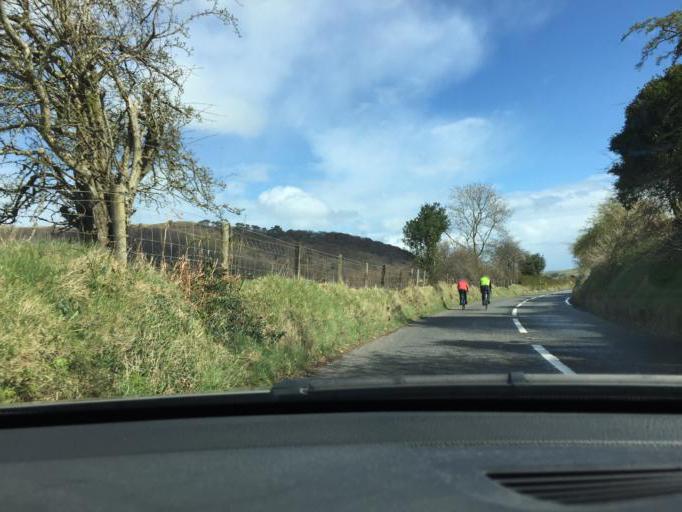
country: GB
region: Northern Ireland
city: Cushendall
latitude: 55.1206
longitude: -6.0925
